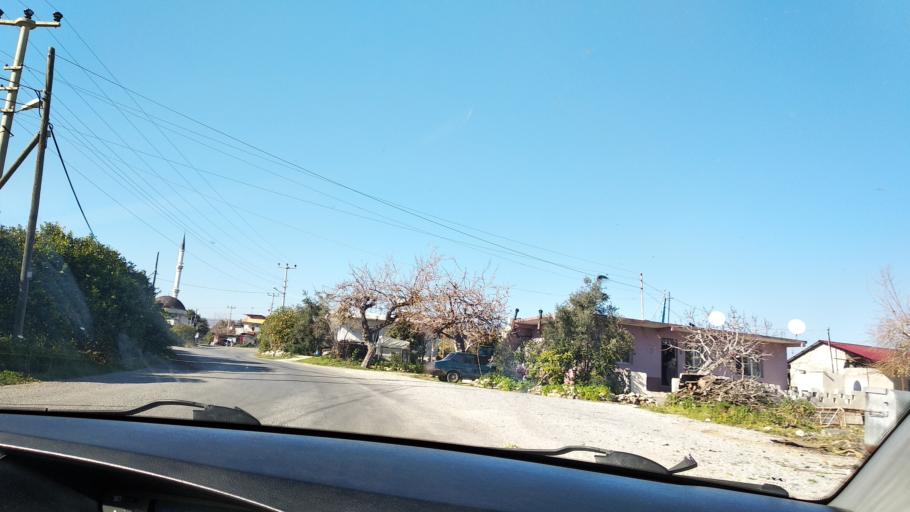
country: TR
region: Mersin
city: Tomuk
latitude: 36.6665
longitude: 34.3595
